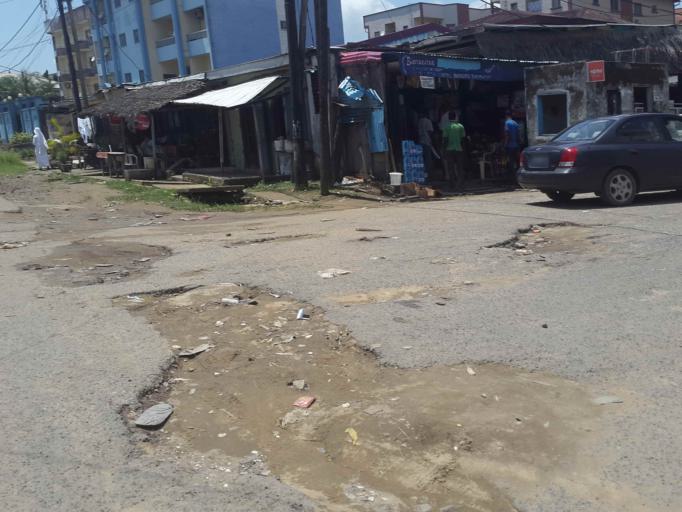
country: CM
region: Littoral
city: Douala
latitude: 4.0902
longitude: 9.7355
